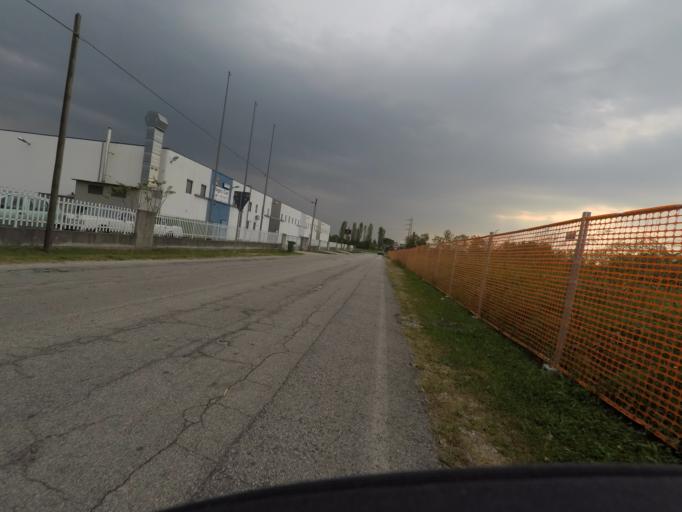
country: IT
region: Friuli Venezia Giulia
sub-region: Provincia di Udine
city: Feletto Umberto
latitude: 46.0994
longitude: 13.2411
